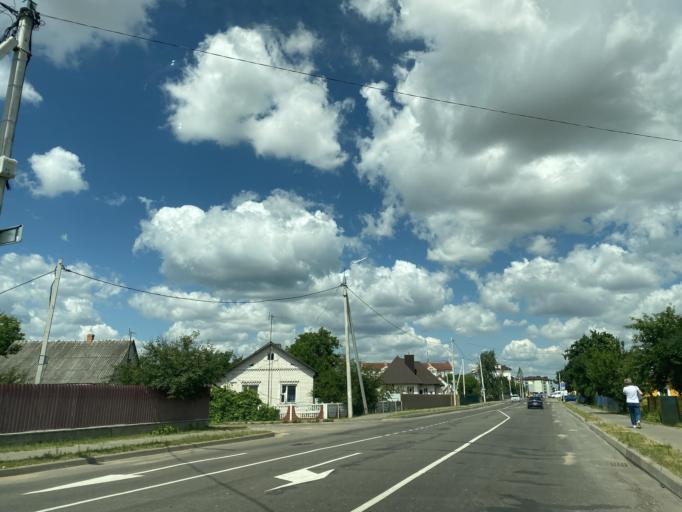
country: BY
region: Brest
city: Ivanava
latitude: 52.1444
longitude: 25.5423
